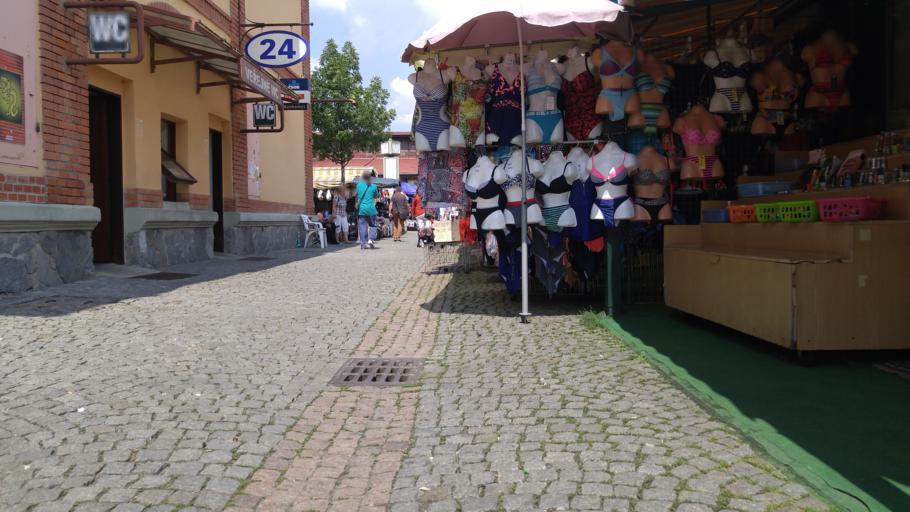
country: CZ
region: Praha
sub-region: Praha 8
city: Karlin
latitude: 50.0986
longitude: 14.4455
